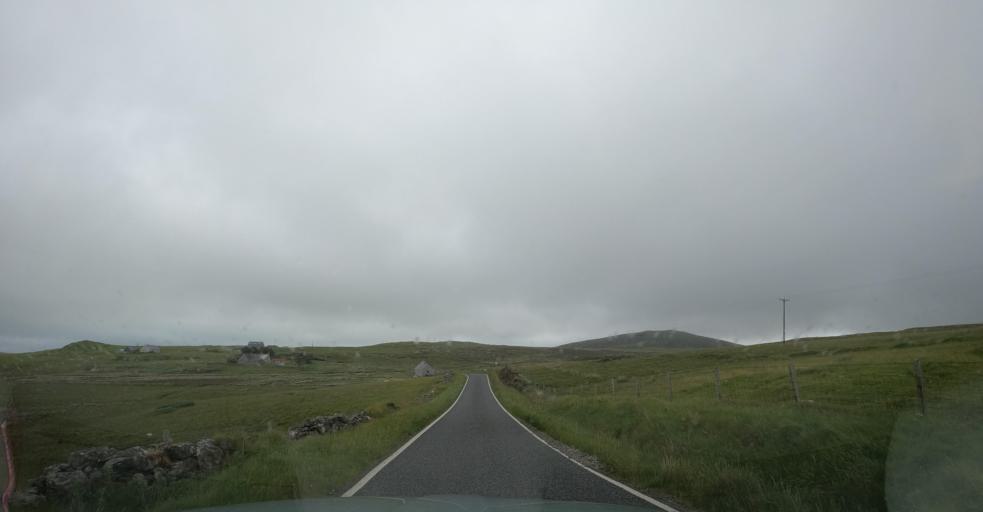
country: GB
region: Scotland
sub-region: Eilean Siar
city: Isle of North Uist
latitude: 57.6603
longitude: -7.2354
